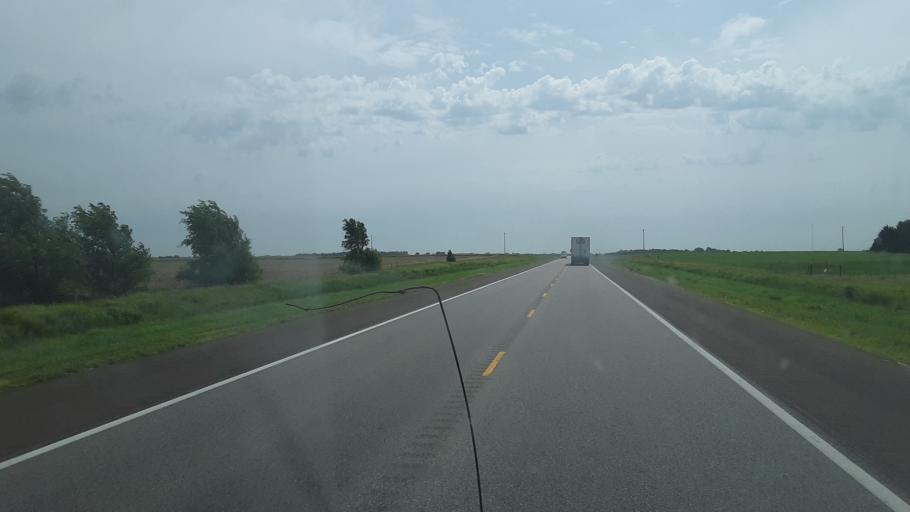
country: US
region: Kansas
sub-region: Reno County
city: Nickerson
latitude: 37.9851
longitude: -98.1092
